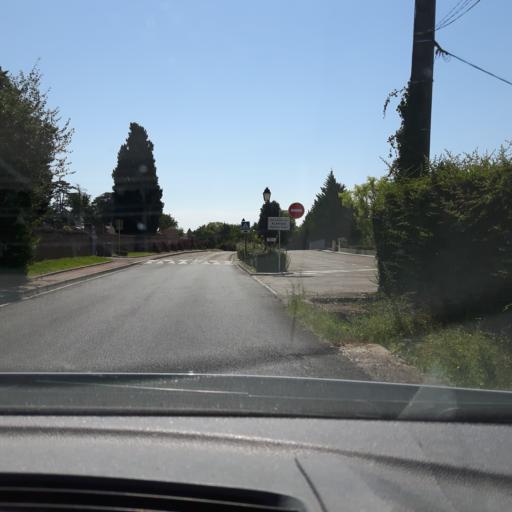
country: FR
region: Midi-Pyrenees
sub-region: Departement de la Haute-Garonne
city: Bouloc
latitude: 43.7826
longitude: 1.4005
